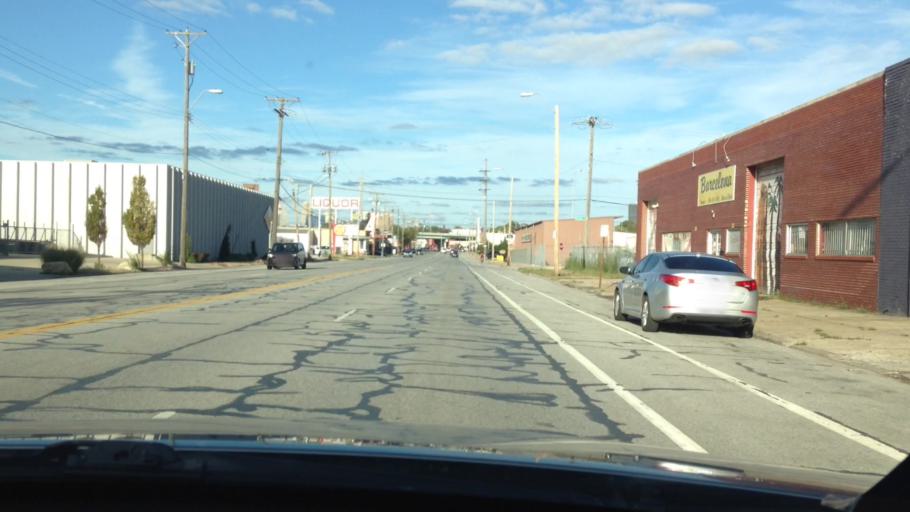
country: US
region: Kansas
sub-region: Johnson County
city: Westwood
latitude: 39.0727
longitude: -94.6069
